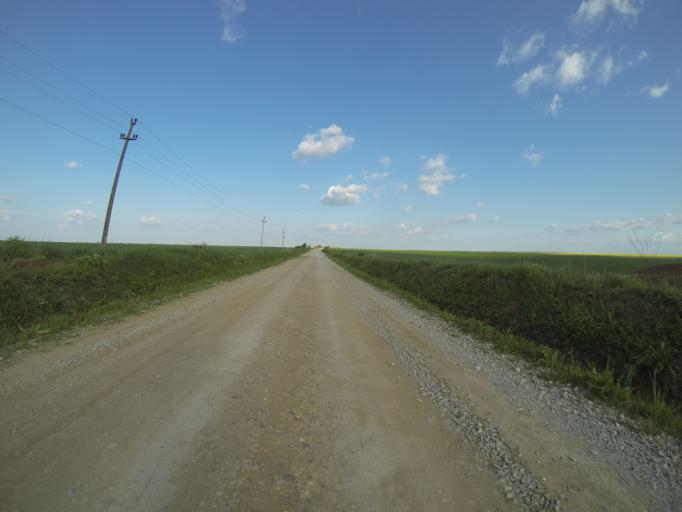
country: RO
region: Dolj
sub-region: Comuna Carpen
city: Carpen
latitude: 44.2913
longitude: 23.3051
